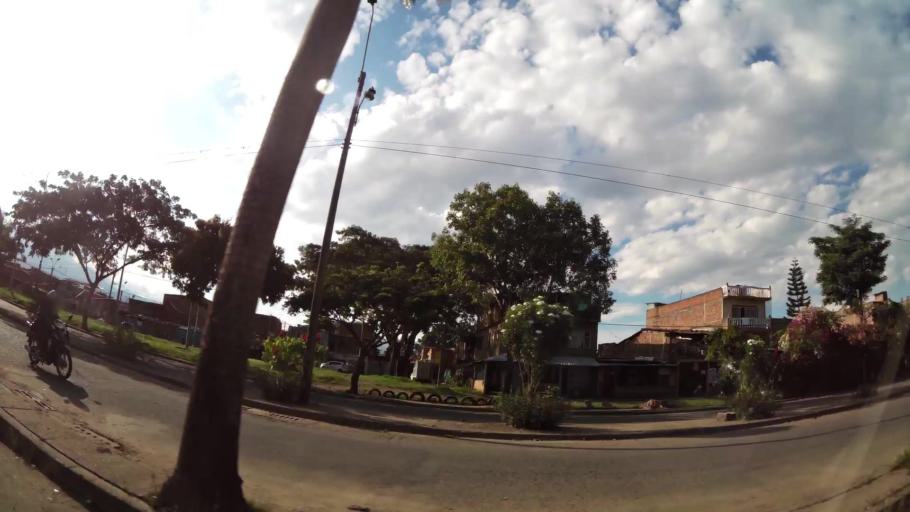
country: CO
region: Valle del Cauca
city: Cali
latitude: 3.4119
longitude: -76.4882
